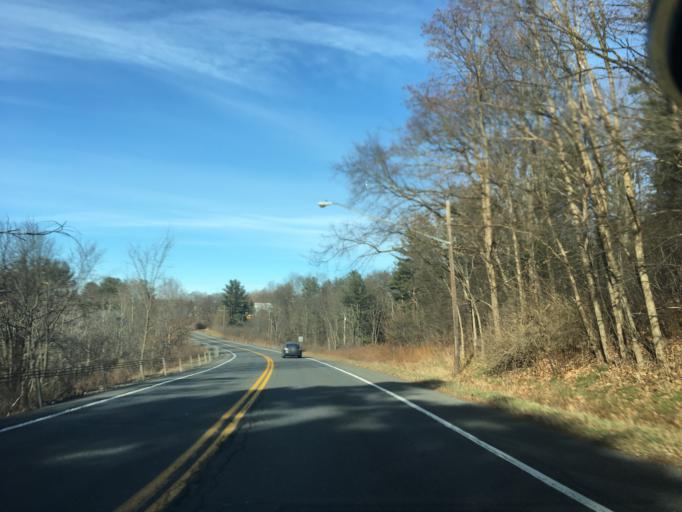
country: US
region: New York
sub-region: Rensselaer County
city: Averill Park
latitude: 42.6384
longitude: -73.5674
